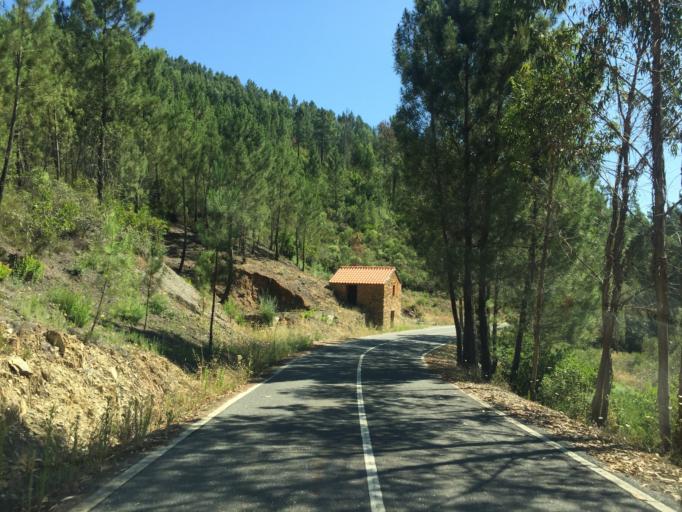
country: PT
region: Coimbra
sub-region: Pampilhosa da Serra
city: Pampilhosa da Serra
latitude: 40.0334
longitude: -7.8192
